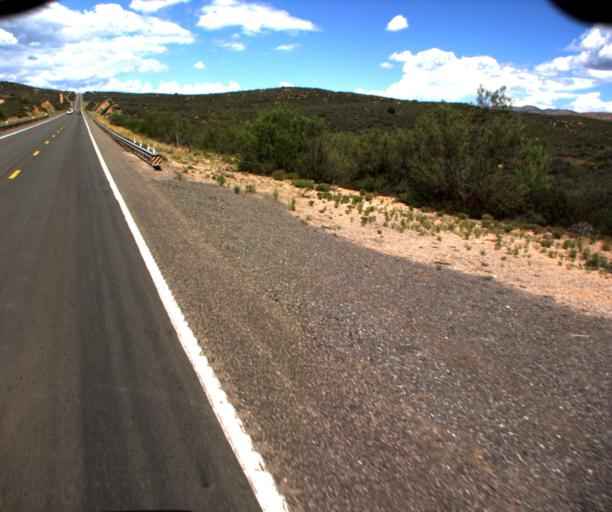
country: US
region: Arizona
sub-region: Yavapai County
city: Dewey-Humboldt
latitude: 34.5295
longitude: -112.1072
